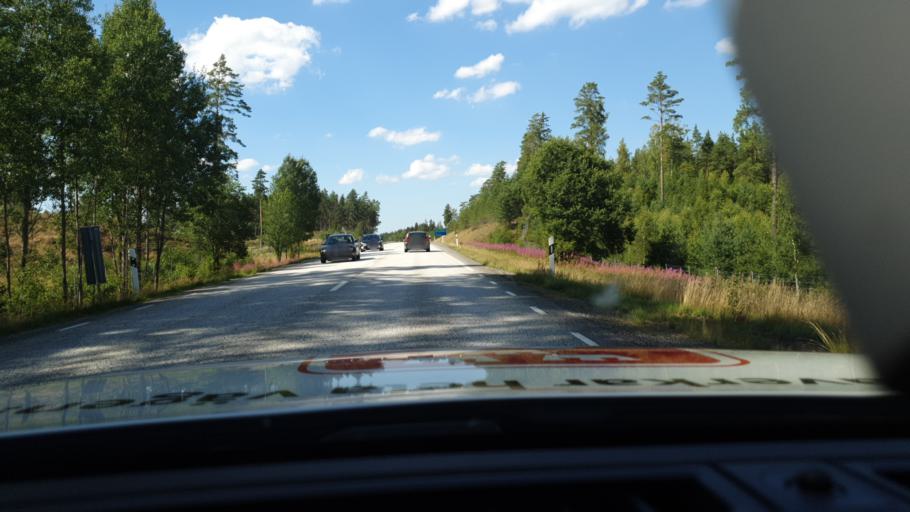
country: SE
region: Joenkoeping
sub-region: Jonkopings Kommun
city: Odensjo
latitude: 57.6123
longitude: 14.2089
